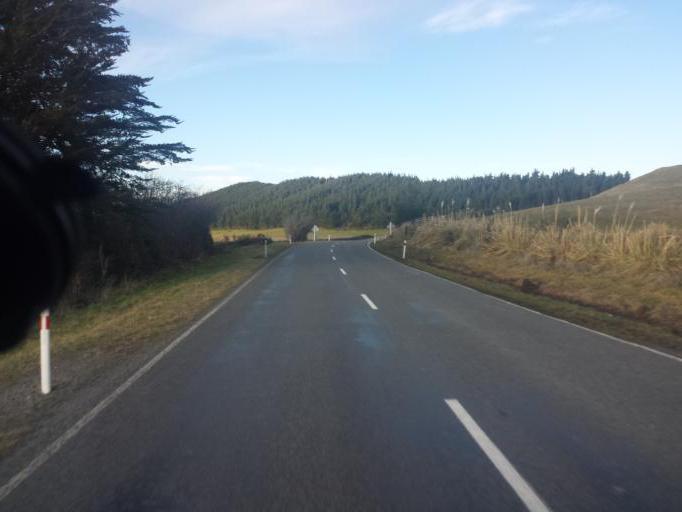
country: NZ
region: Canterbury
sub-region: Ashburton District
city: Methven
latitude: -43.5191
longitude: 171.8436
